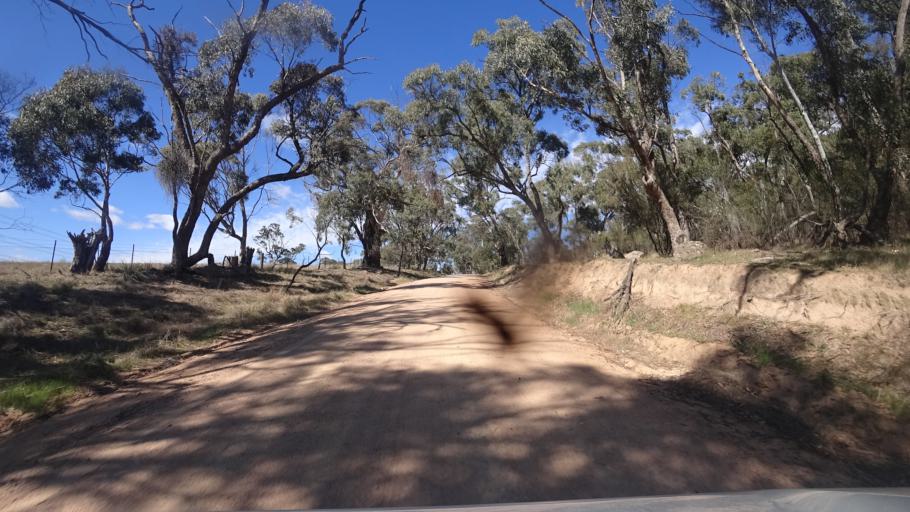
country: AU
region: New South Wales
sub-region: Oberon
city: Oberon
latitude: -33.5370
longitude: 149.9330
